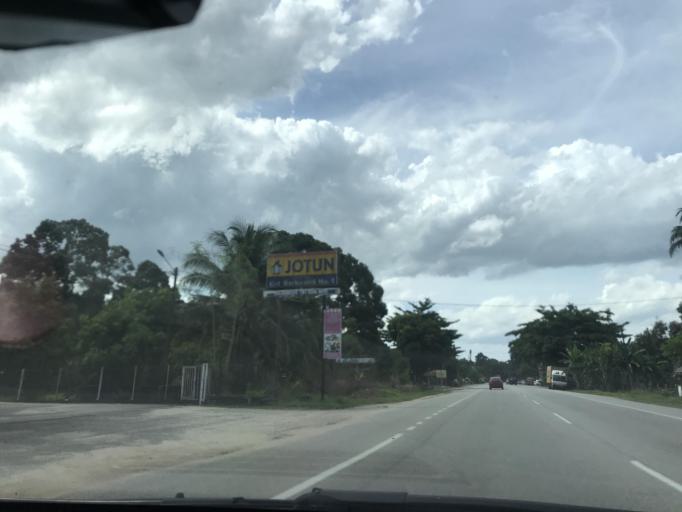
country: MY
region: Kelantan
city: Kampong Pangkal Kalong
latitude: 5.9137
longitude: 102.1879
